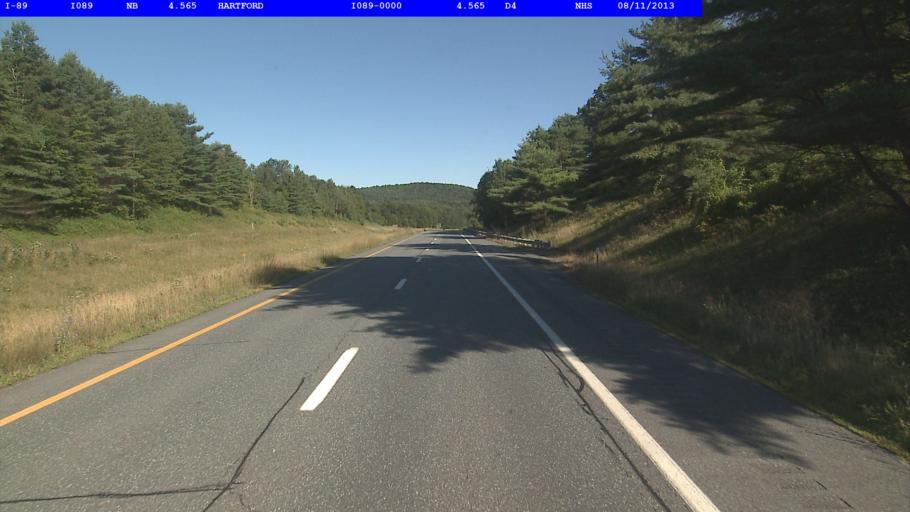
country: US
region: Vermont
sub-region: Windsor County
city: White River Junction
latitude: 43.6736
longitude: -72.3936
